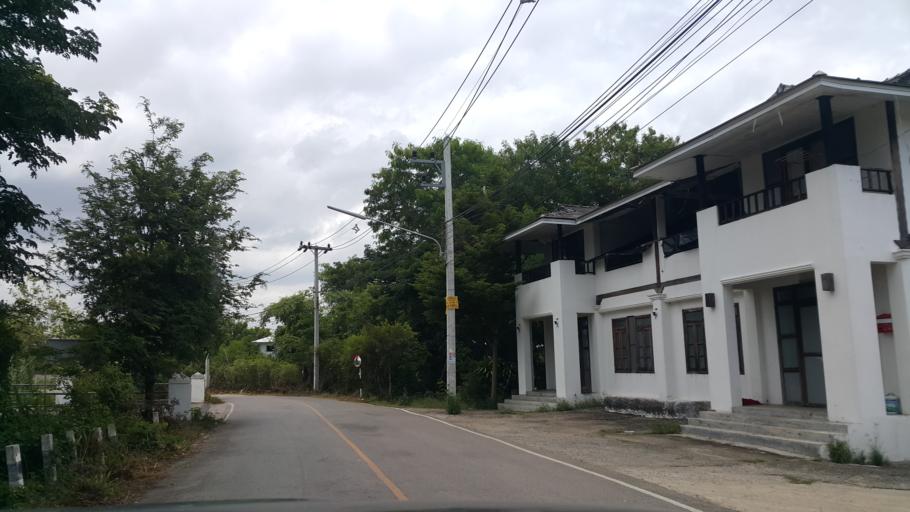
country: TH
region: Chiang Mai
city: Saraphi
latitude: 18.7088
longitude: 98.9770
